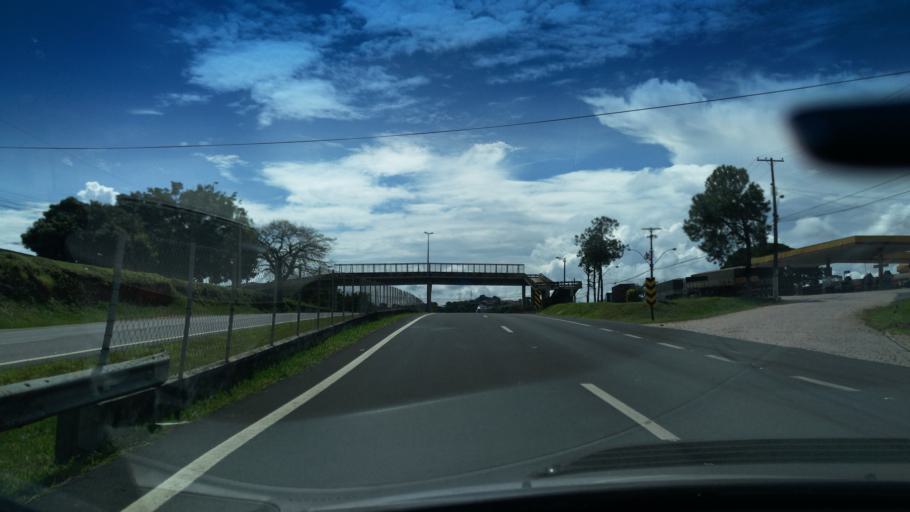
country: BR
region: Sao Paulo
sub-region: Santo Antonio Do Jardim
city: Espirito Santo do Pinhal
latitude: -22.1936
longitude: -46.7717
